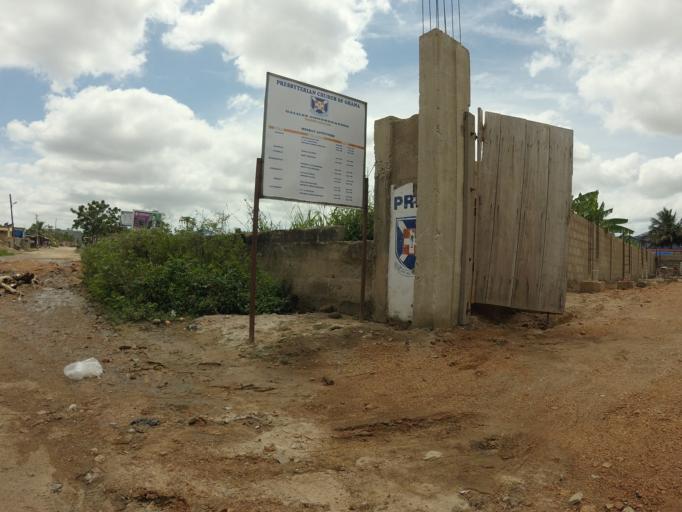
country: GH
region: Central
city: Kasoa
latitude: 5.5506
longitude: -0.3984
